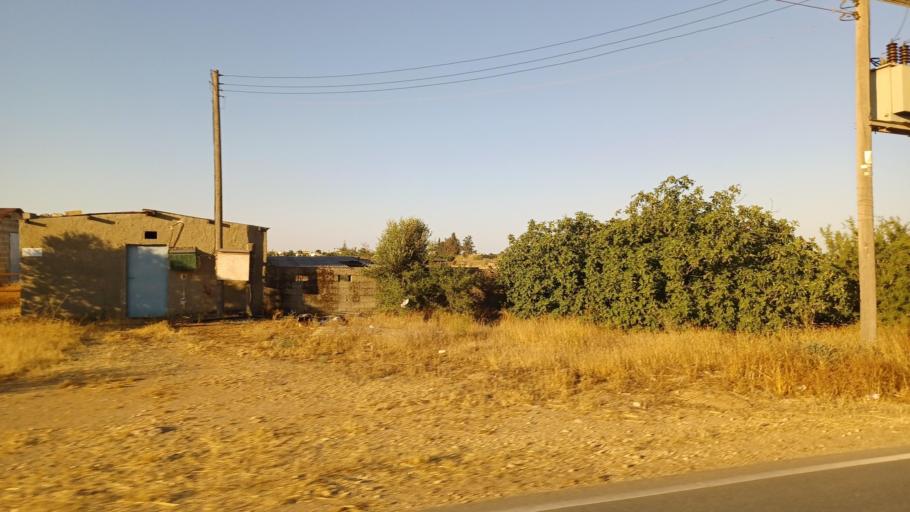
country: CY
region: Ammochostos
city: Achna
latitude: 35.0359
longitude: 33.7822
